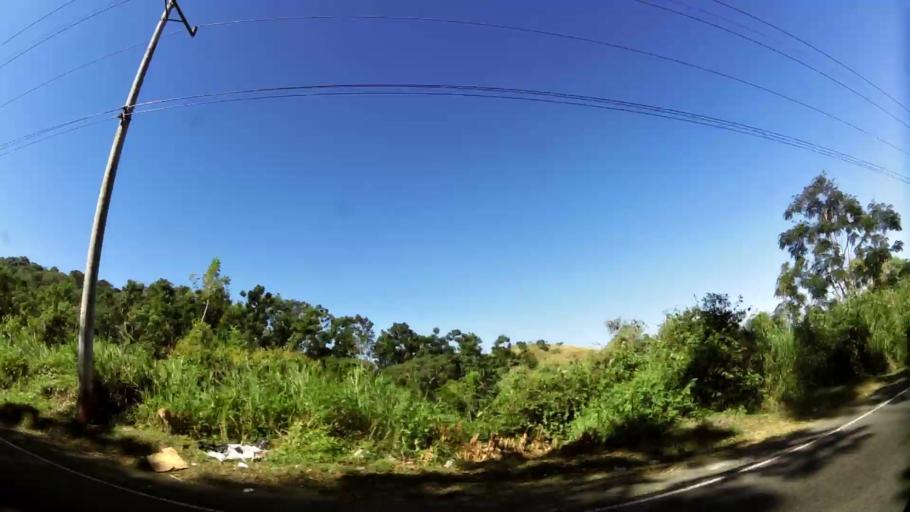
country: SV
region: Ahuachapan
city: Ahuachapan
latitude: 13.8967
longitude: -89.8356
